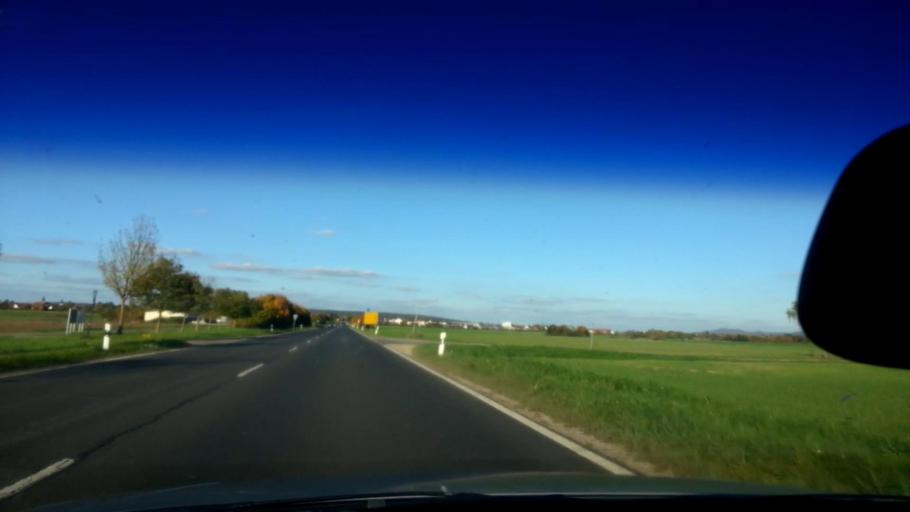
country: DE
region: Bavaria
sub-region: Upper Franconia
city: Rattelsdorf
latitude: 50.0022
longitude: 10.8872
